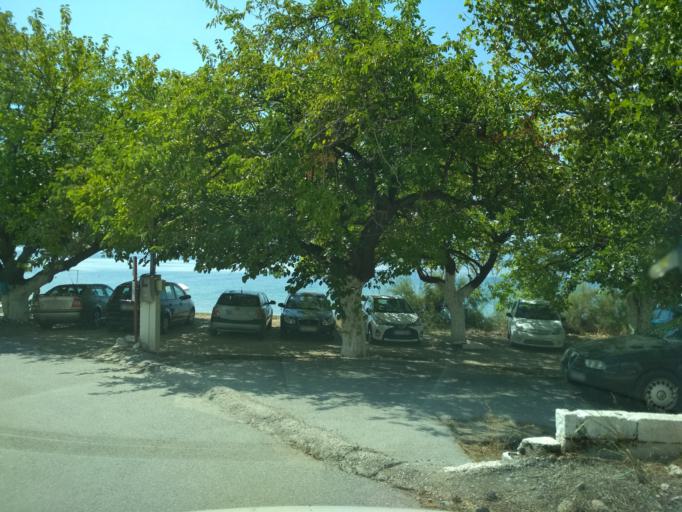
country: GR
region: Central Greece
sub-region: Nomos Evvoias
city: Roviai
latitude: 38.8124
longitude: 23.2262
